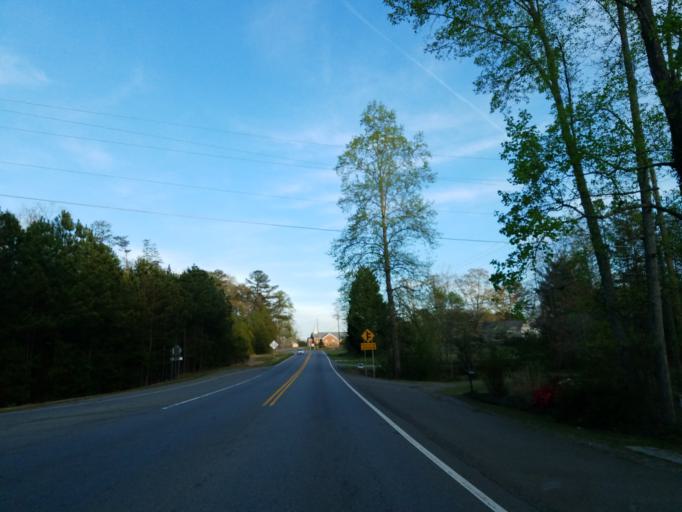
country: US
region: Georgia
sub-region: Cherokee County
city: Canton
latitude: 34.2215
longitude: -84.4685
